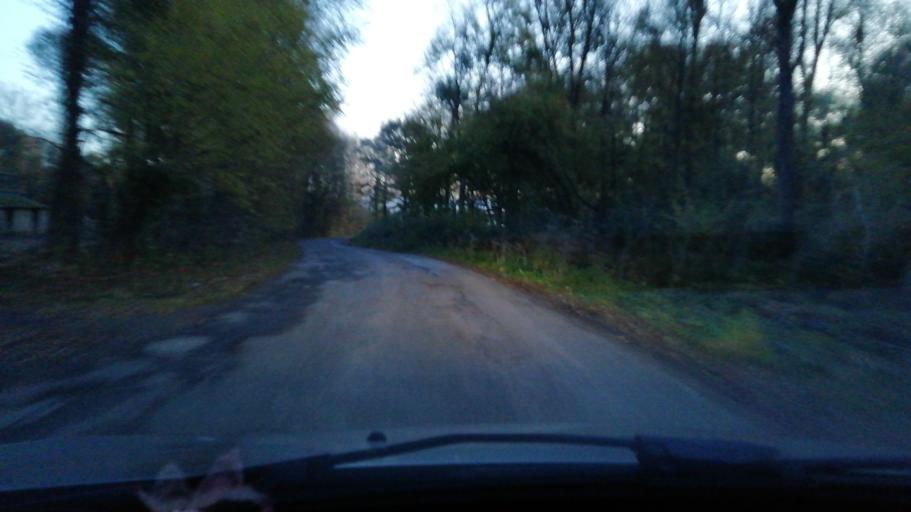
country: FR
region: Nord-Pas-de-Calais
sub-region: Departement du Nord
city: Marpent
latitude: 50.2763
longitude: 4.0886
